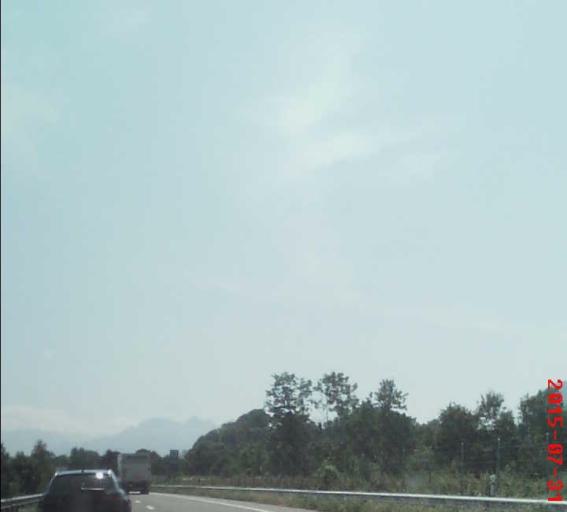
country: AT
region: Vorarlberg
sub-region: Politischer Bezirk Feldkirch
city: Koblach
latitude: 47.3472
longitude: 9.5977
